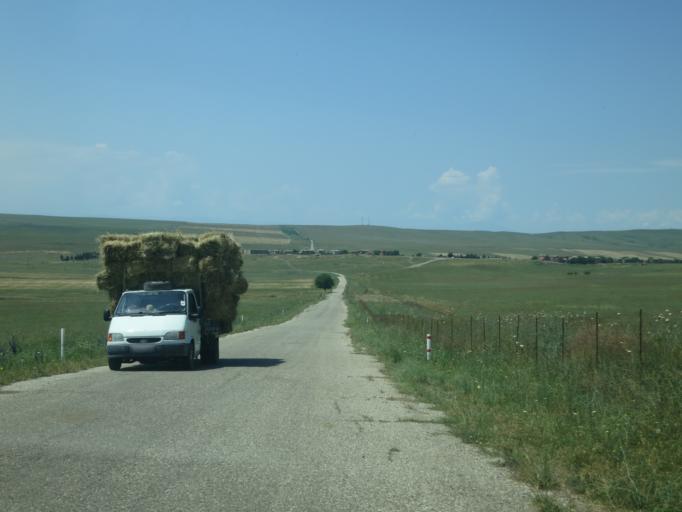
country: GE
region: Kakheti
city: Sagarejo
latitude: 41.5136
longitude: 45.3964
